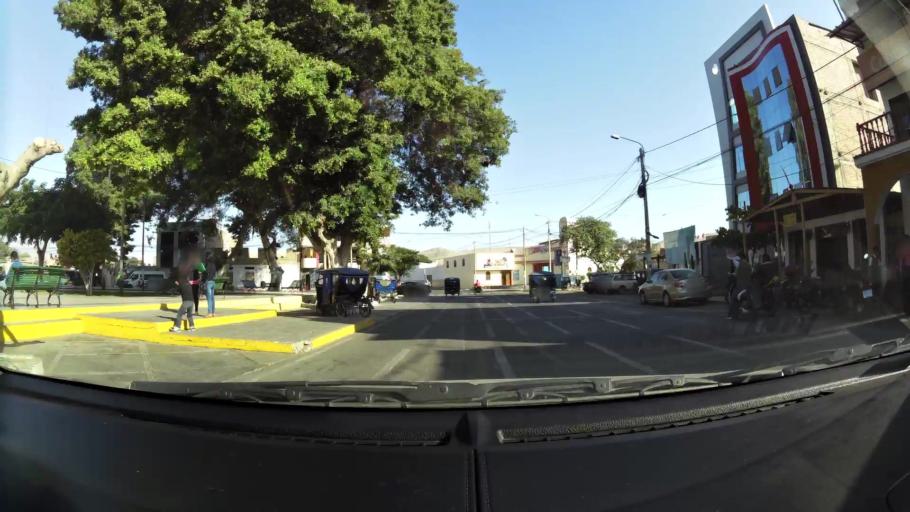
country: PE
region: Ancash
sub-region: Provincia de Casma
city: Casma
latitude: -9.4759
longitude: -78.3059
